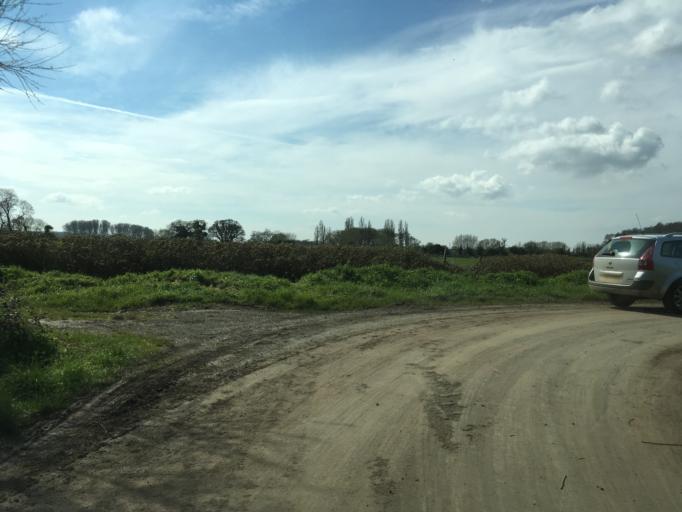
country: GB
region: England
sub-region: South Gloucestershire
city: Almondsbury
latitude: 51.5647
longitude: -2.5809
